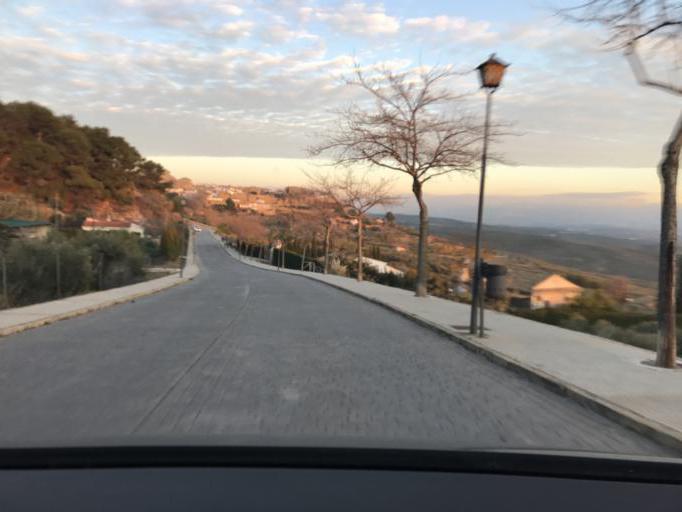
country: ES
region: Andalusia
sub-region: Provincia de Jaen
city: Ubeda
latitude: 38.0052
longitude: -3.3755
